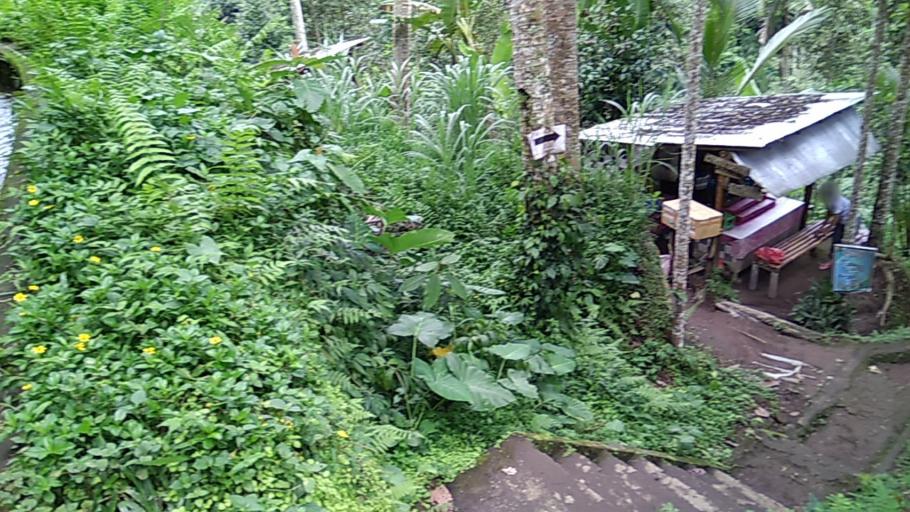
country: ID
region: Bali
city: Banjar Kubu
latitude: -8.4410
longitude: 115.3884
